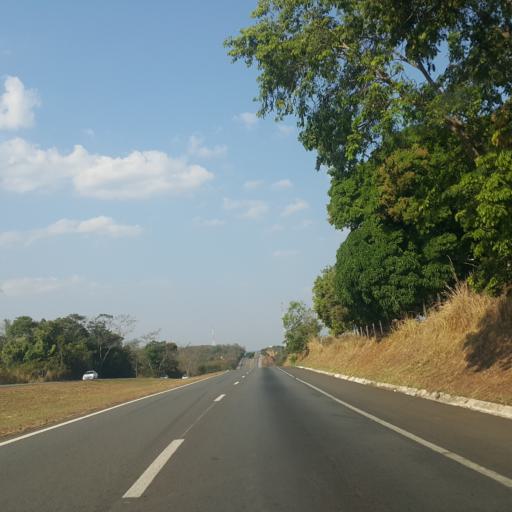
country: BR
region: Goias
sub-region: Abadiania
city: Abadiania
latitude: -16.1635
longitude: -48.6310
